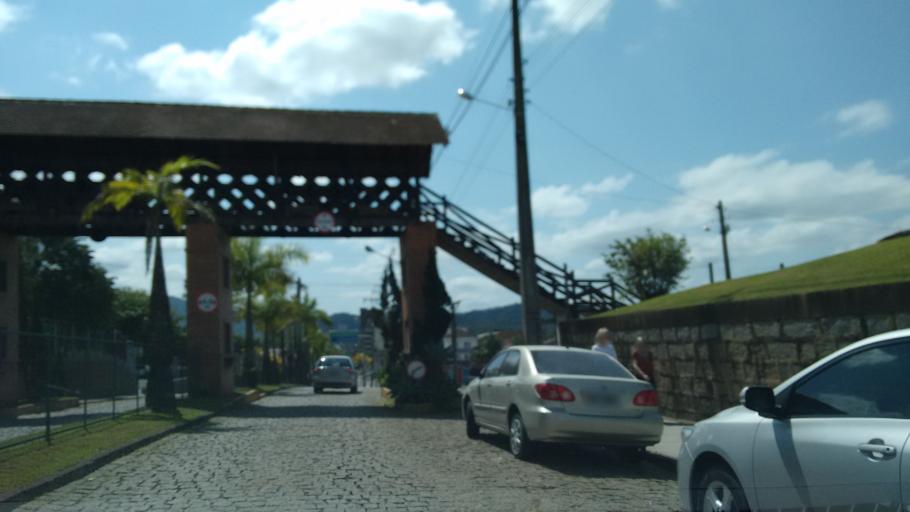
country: BR
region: Santa Catarina
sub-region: Pomerode
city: Pomerode
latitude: -26.7388
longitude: -49.1783
